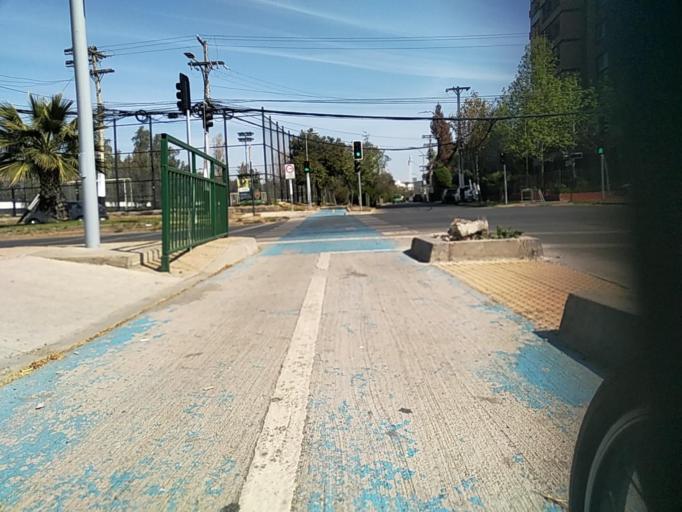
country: CL
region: Santiago Metropolitan
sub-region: Provincia de Santiago
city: Villa Presidente Frei, Nunoa, Santiago, Chile
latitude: -33.5015
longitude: -70.6061
